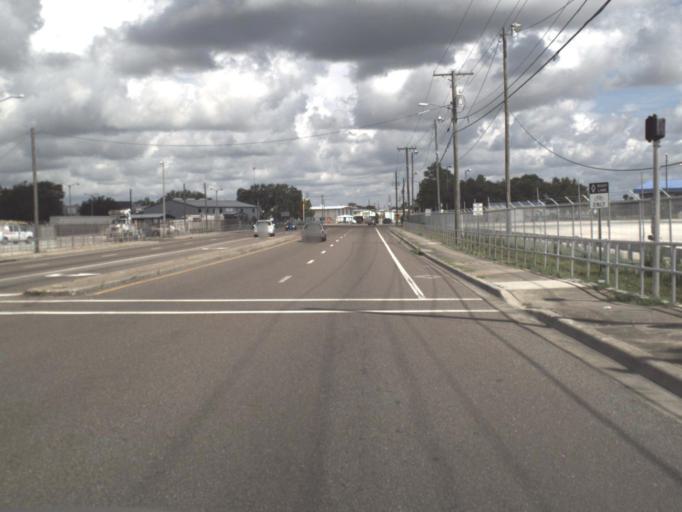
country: US
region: Florida
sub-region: Hillsborough County
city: Egypt Lake-Leto
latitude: 28.0110
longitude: -82.5321
